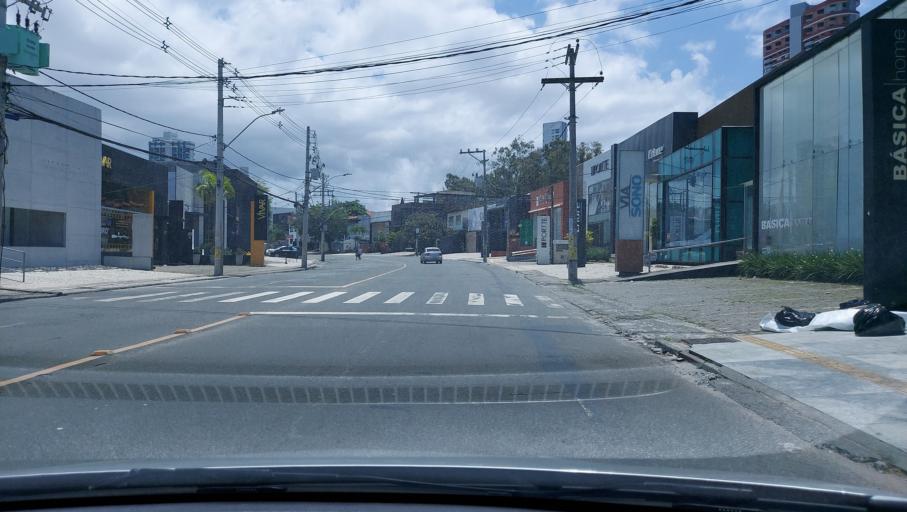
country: BR
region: Bahia
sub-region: Salvador
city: Salvador
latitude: -12.9854
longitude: -38.4574
